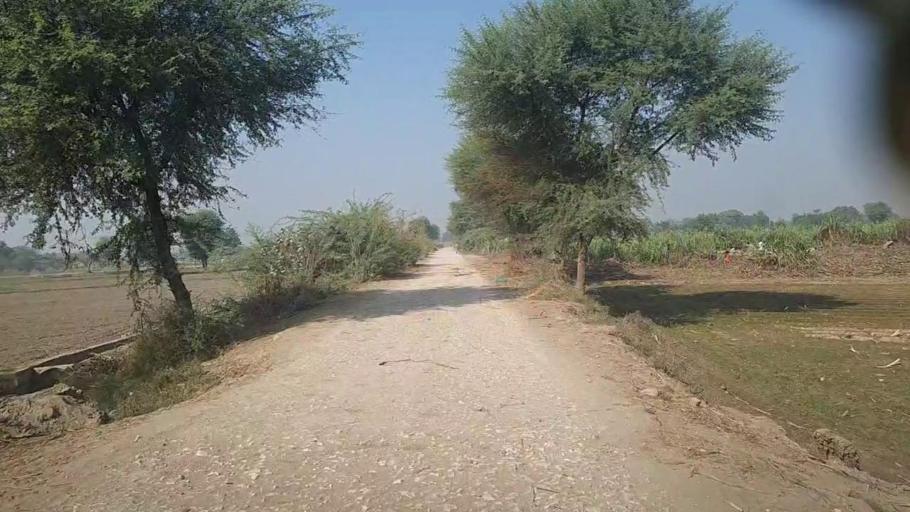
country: PK
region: Sindh
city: Karaundi
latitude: 26.9729
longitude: 68.4524
